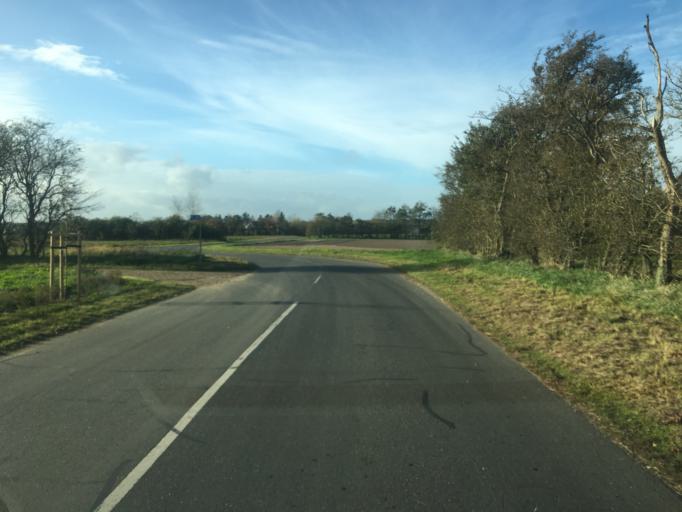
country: DK
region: South Denmark
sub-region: Tonder Kommune
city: Logumkloster
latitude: 55.0711
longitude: 8.9466
